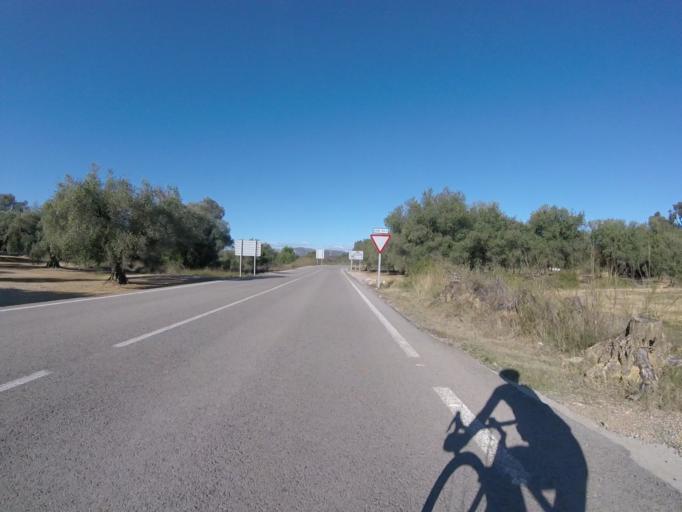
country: ES
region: Valencia
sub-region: Provincia de Castello
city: Cervera del Maestre
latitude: 40.4770
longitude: 0.2186
